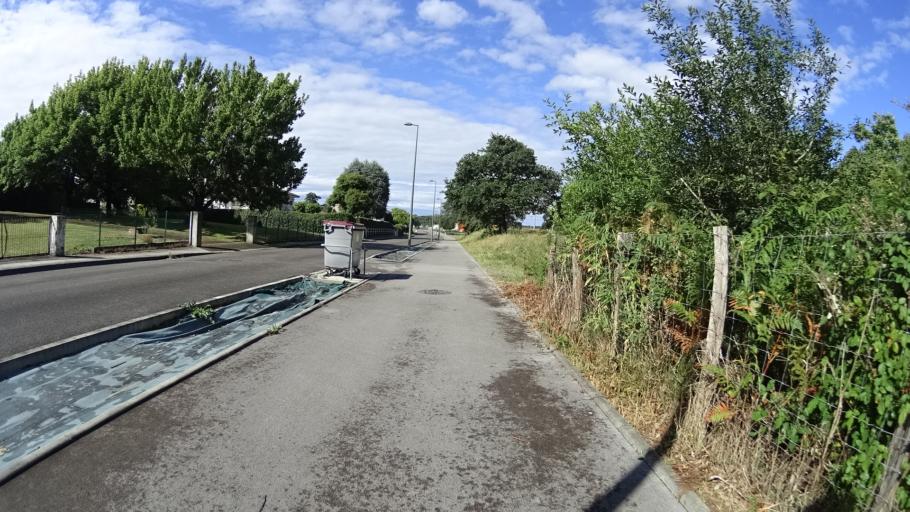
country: FR
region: Aquitaine
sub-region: Departement des Landes
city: Dax
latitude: 43.6965
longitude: -1.0776
